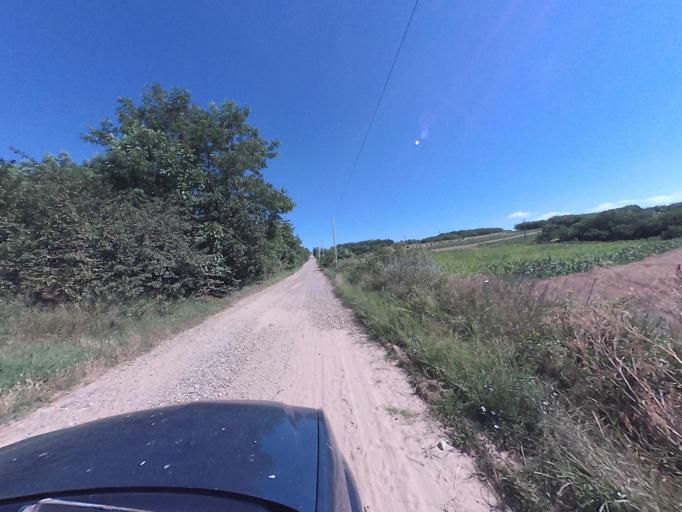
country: RO
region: Vaslui
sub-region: Comuna Costesti
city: Costesti
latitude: 46.4823
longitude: 27.7691
